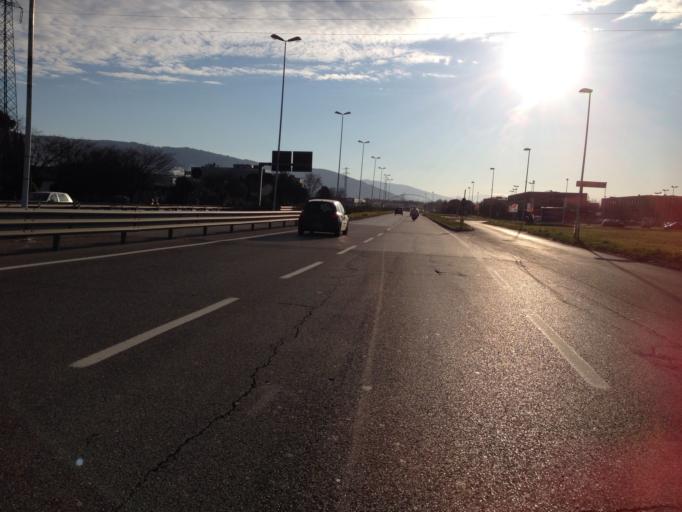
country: IT
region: Tuscany
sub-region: Provincia di Prato
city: Prato
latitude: 43.8783
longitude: 11.0660
